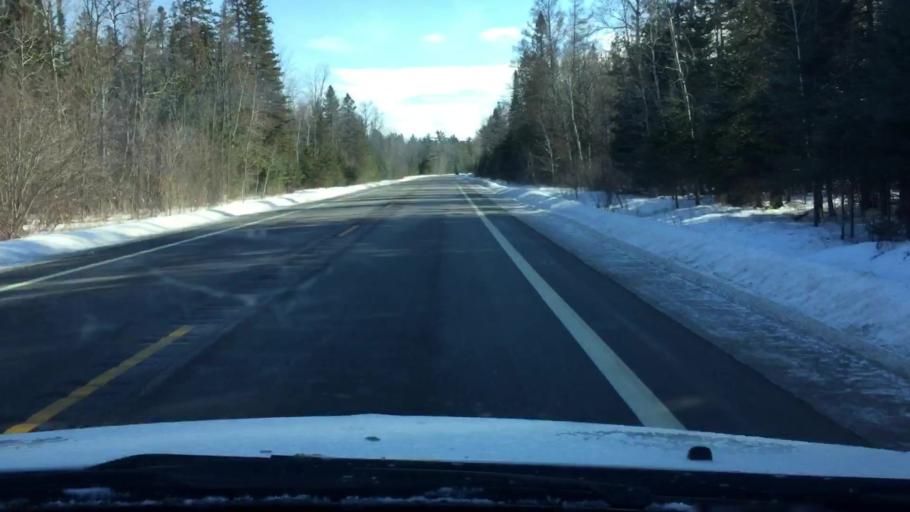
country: US
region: Michigan
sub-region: Charlevoix County
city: East Jordan
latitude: 45.0580
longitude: -85.0756
